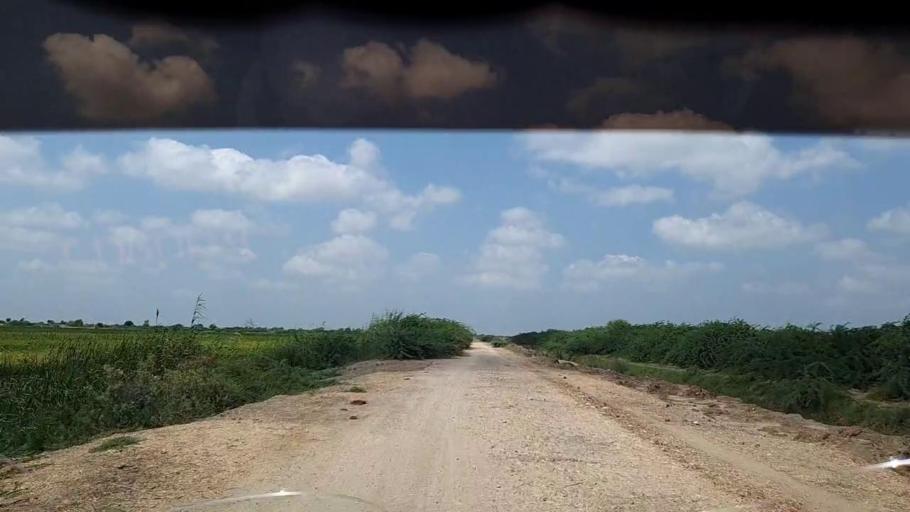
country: PK
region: Sindh
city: Kadhan
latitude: 24.5924
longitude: 68.9661
